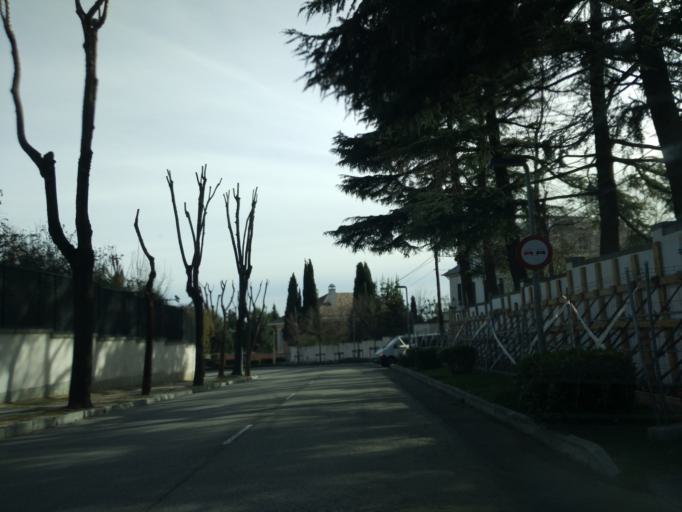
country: ES
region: Madrid
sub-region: Provincia de Madrid
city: Tetuan de las Victorias
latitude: 40.4640
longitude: -3.7309
